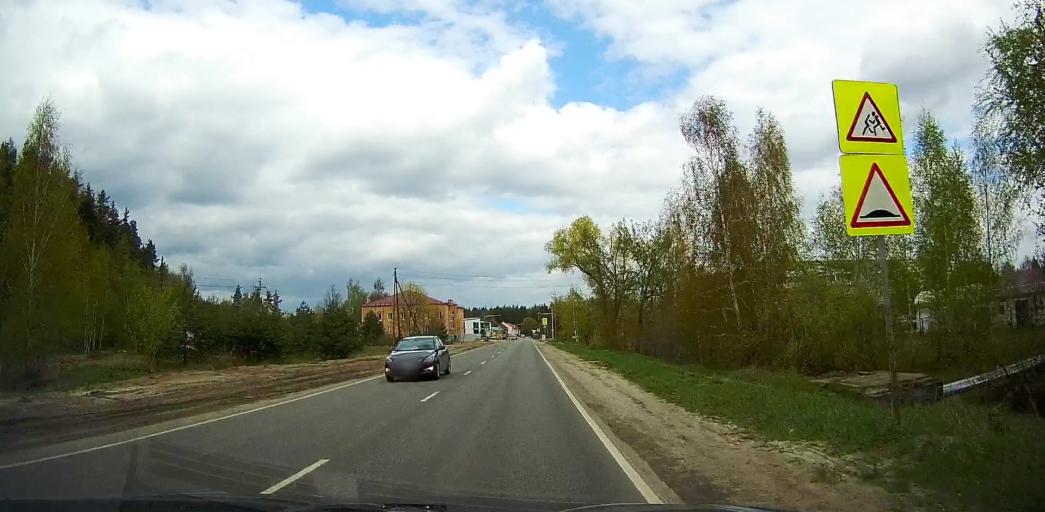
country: RU
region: Moskovskaya
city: Ashitkovo
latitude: 55.4347
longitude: 38.5787
